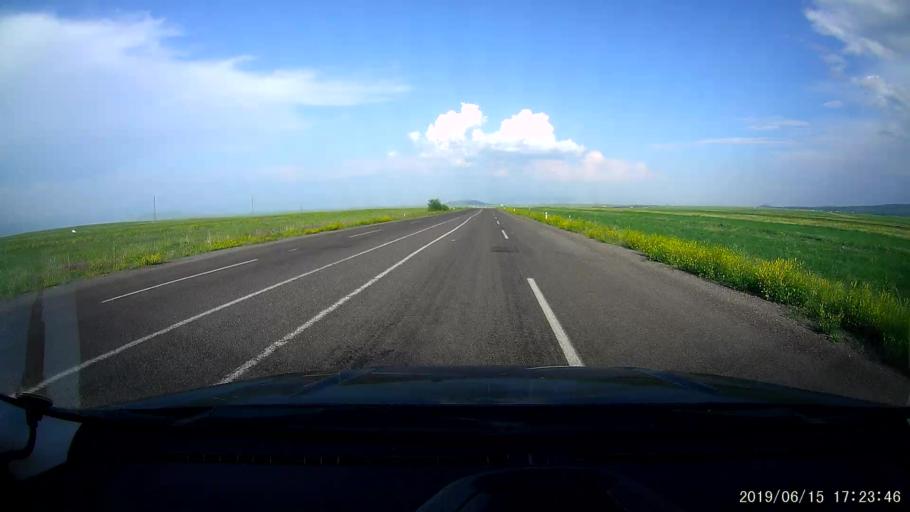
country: TR
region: Kars
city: Basgedikler
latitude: 40.6165
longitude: 43.3700
